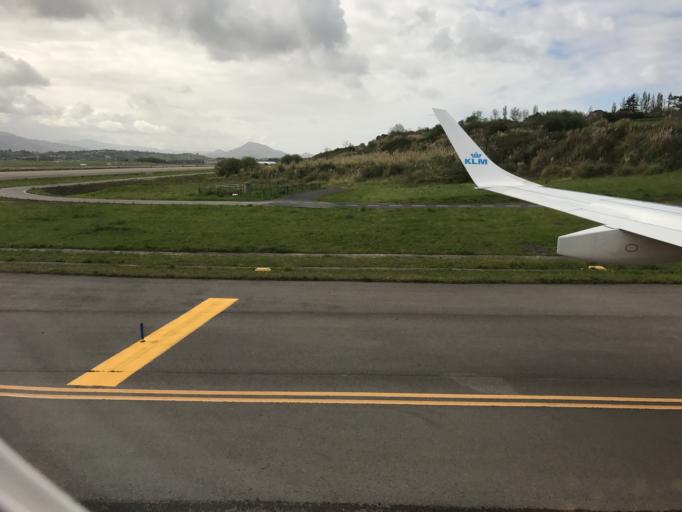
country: ES
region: Basque Country
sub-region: Bizkaia
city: Sondika
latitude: 43.3034
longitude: -2.9101
